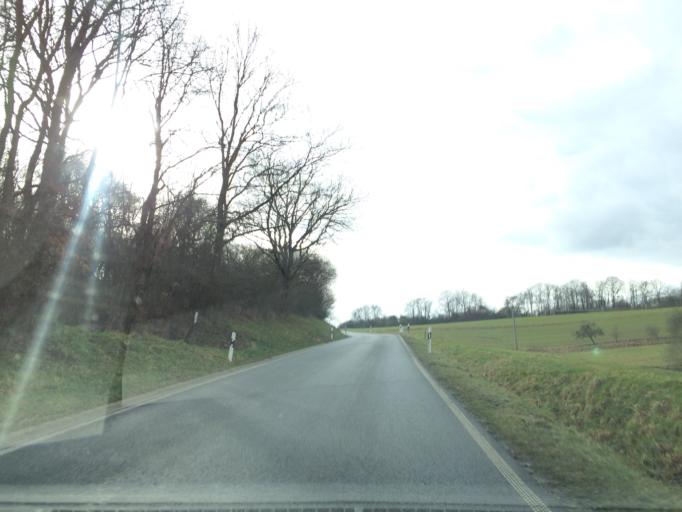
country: DE
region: Hesse
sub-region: Regierungsbezirk Darmstadt
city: Gravenwiesbach
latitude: 50.3586
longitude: 8.4318
